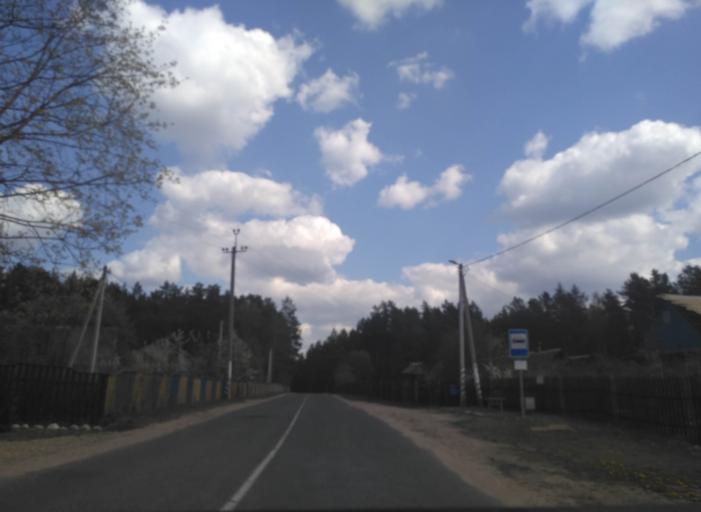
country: BY
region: Minsk
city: Radashkovichy
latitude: 54.1841
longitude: 27.2555
